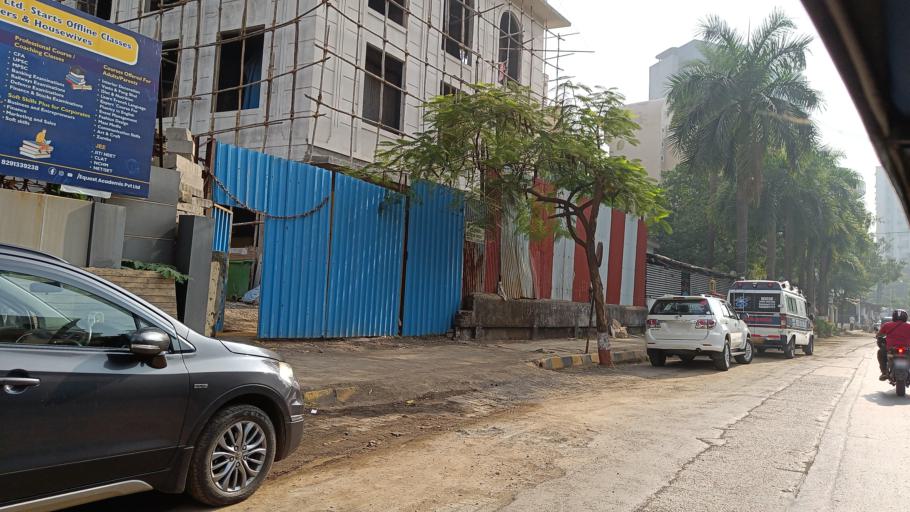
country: IN
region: Maharashtra
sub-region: Mumbai Suburban
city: Mumbai
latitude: 19.1152
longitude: 72.8356
